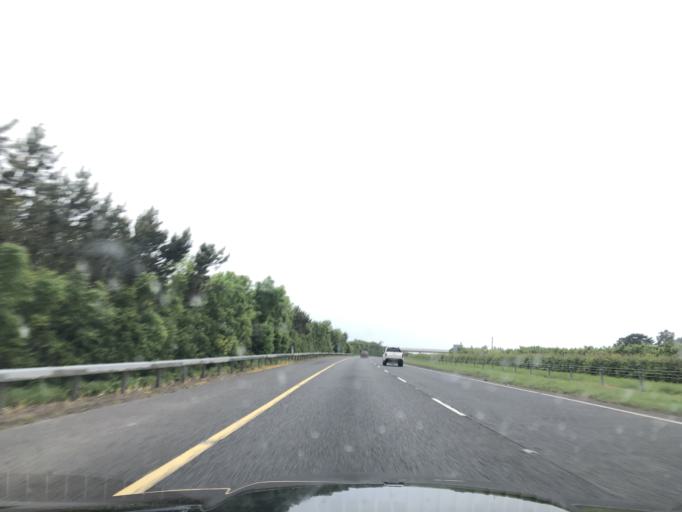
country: IE
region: Leinster
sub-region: Lu
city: Tullyallen
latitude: 53.7471
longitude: -6.4076
